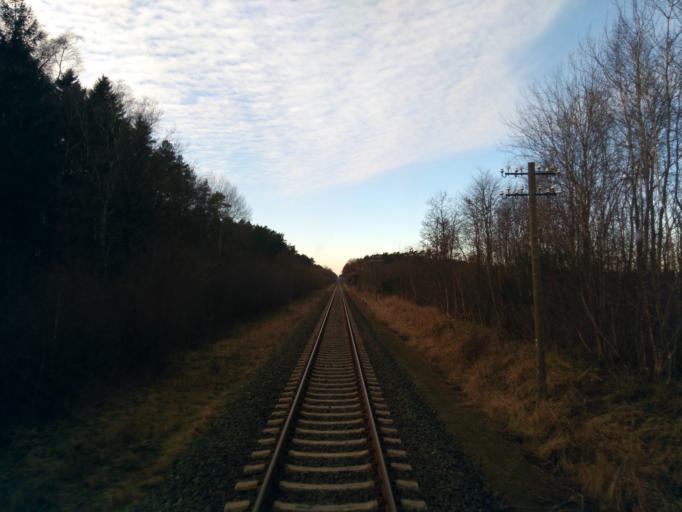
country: DE
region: Lower Saxony
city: Hanstedt Eins
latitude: 53.0114
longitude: 10.3595
